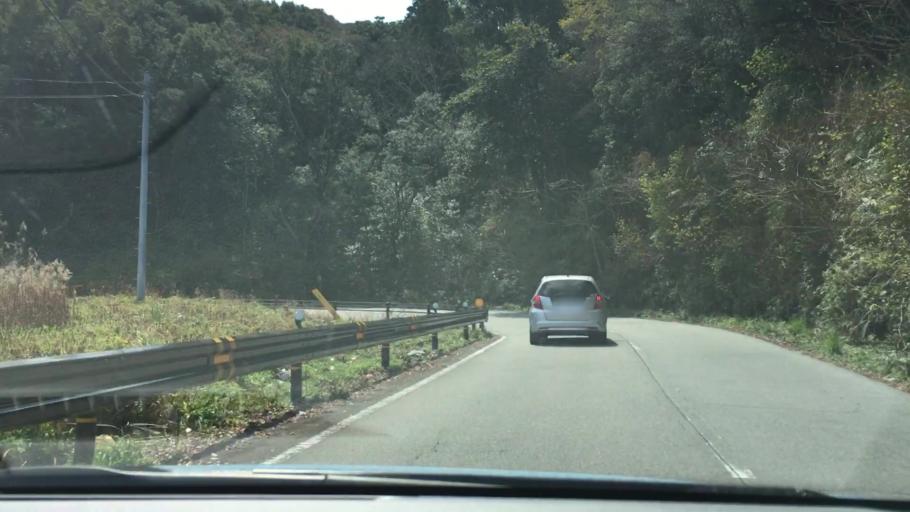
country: JP
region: Mie
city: Toba
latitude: 34.4541
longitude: 136.8732
